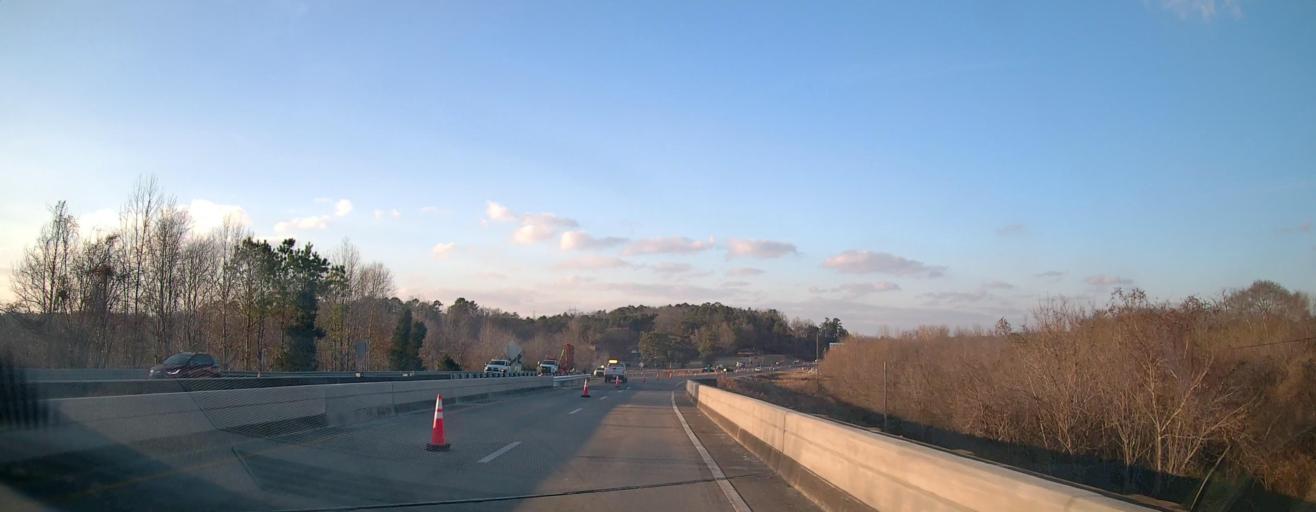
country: US
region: Alabama
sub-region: Calhoun County
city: Saks
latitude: 33.7217
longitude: -85.8749
